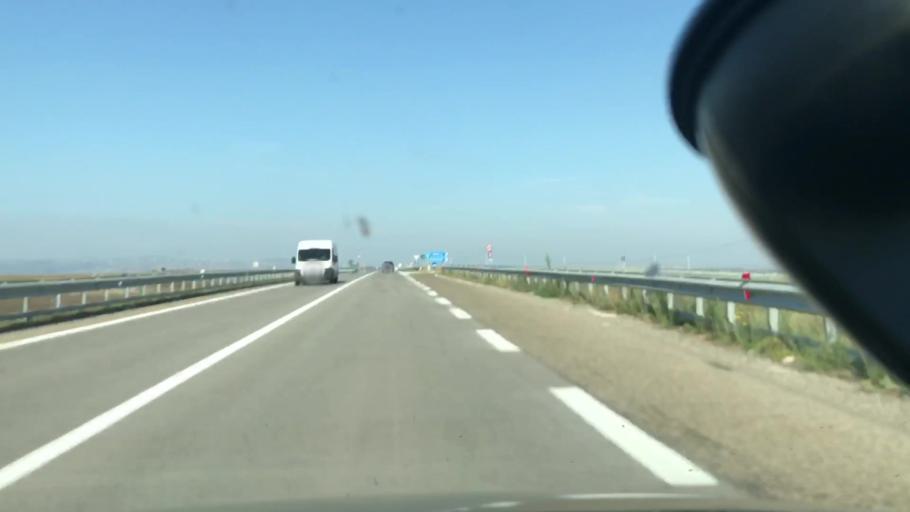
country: IT
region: Basilicate
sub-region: Provincia di Potenza
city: Venosa
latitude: 40.9932
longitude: 15.8902
